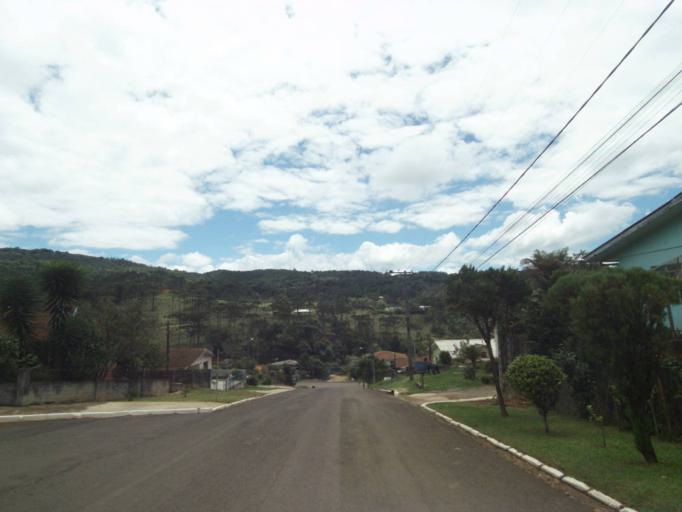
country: BR
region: Parana
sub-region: Pinhao
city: Pinhao
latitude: -26.1579
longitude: -51.5602
